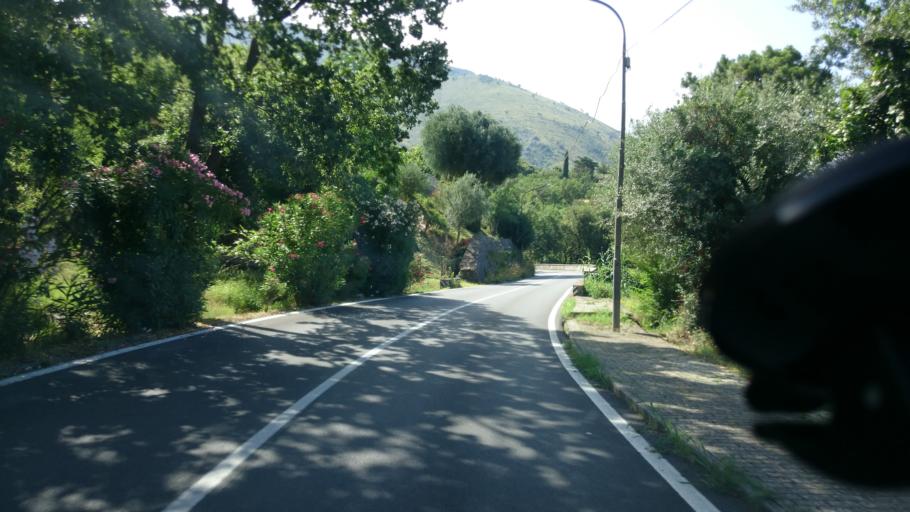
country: IT
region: Basilicate
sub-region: Provincia di Potenza
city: Maratea
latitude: 40.0343
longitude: 15.6721
